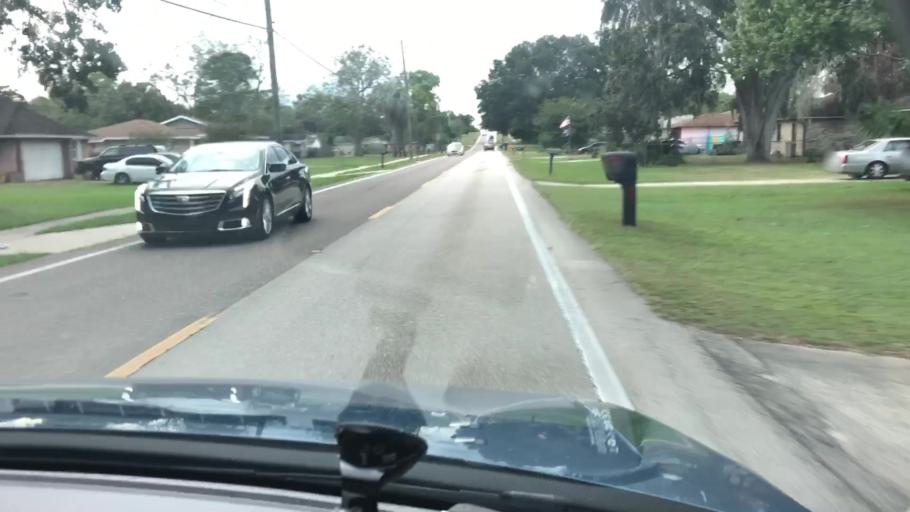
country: US
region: Florida
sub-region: Polk County
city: Gibsonia
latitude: 28.1356
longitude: -81.9959
